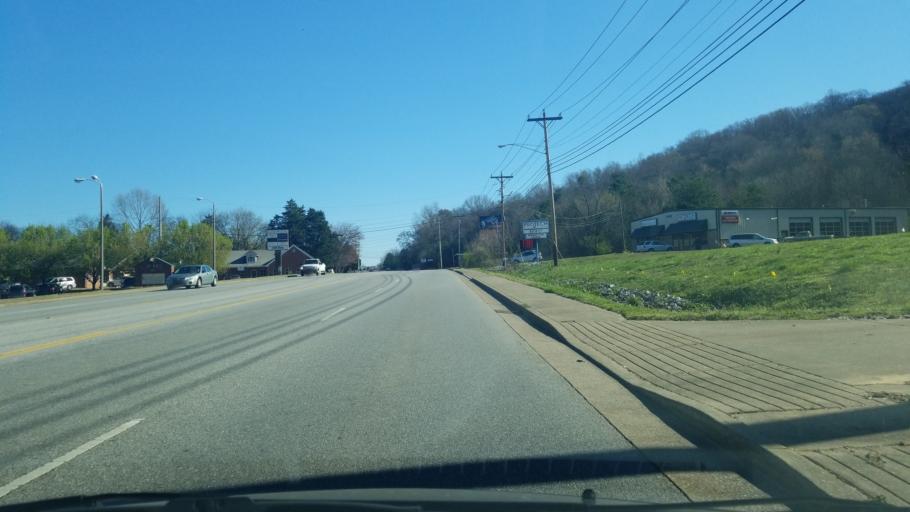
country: US
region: Tennessee
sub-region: Hamilton County
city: Middle Valley
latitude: 35.1581
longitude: -85.1952
